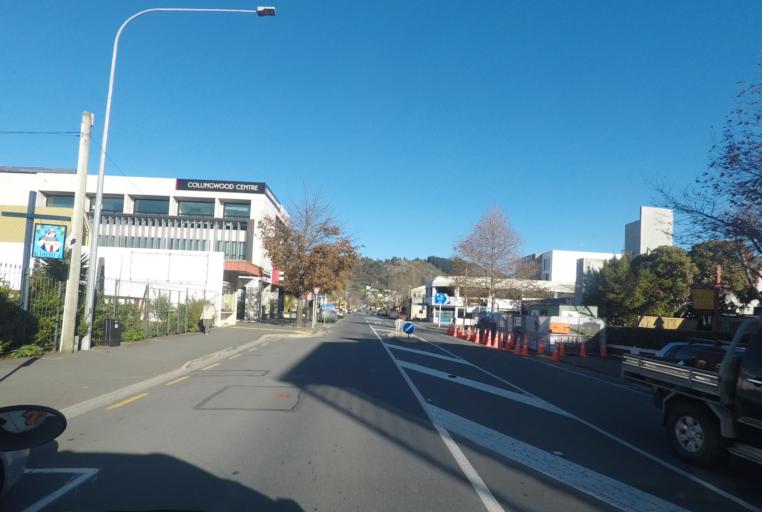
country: NZ
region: Nelson
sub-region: Nelson City
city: Nelson
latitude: -41.2732
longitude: 173.2870
